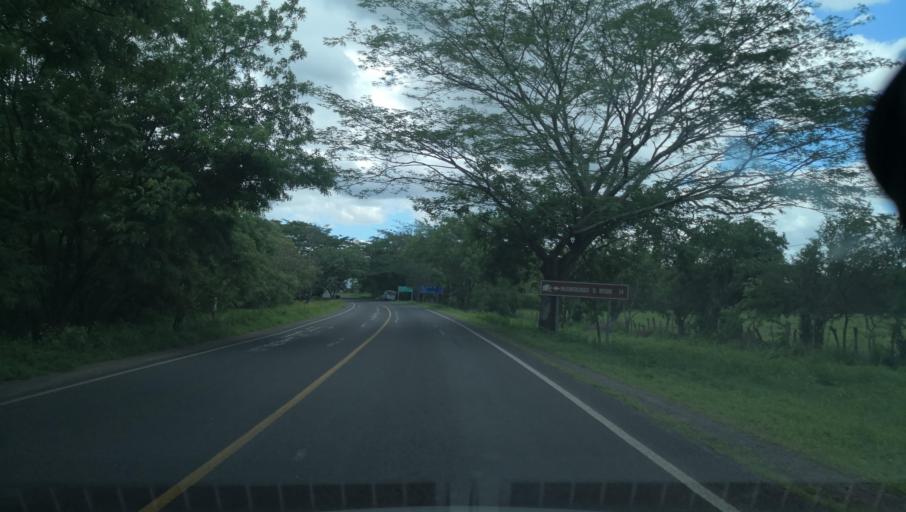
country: NI
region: Madriz
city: Palacaguina
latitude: 13.4309
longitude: -86.4083
